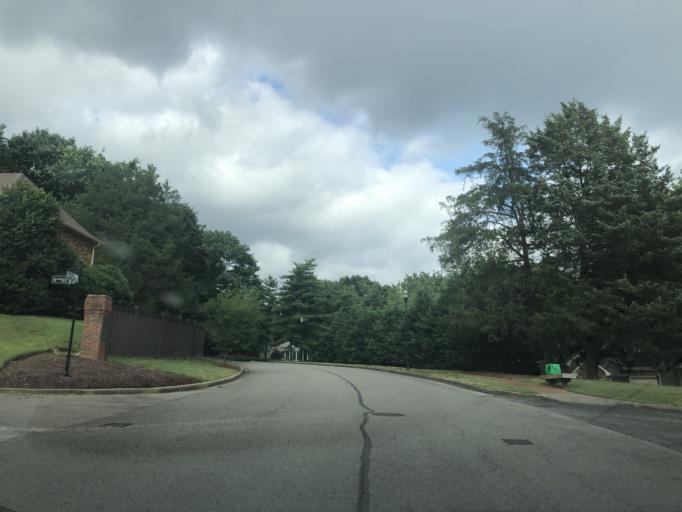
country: US
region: Tennessee
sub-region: Davidson County
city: Oak Hill
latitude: 36.0952
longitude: -86.8155
